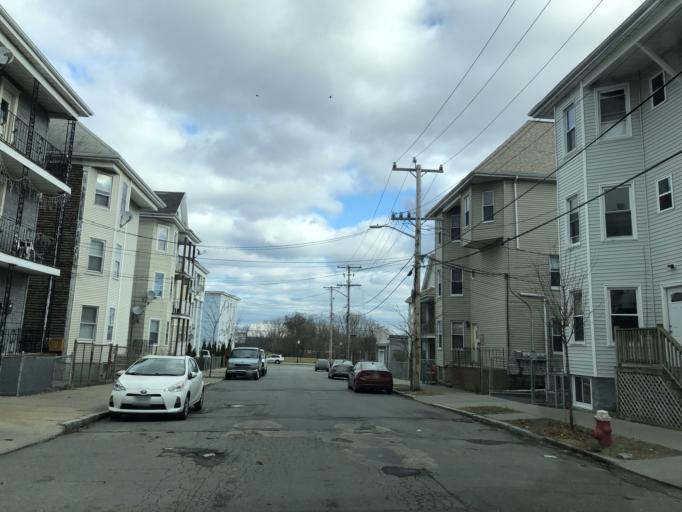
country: US
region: Massachusetts
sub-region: Bristol County
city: New Bedford
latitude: 41.6587
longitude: -70.9252
